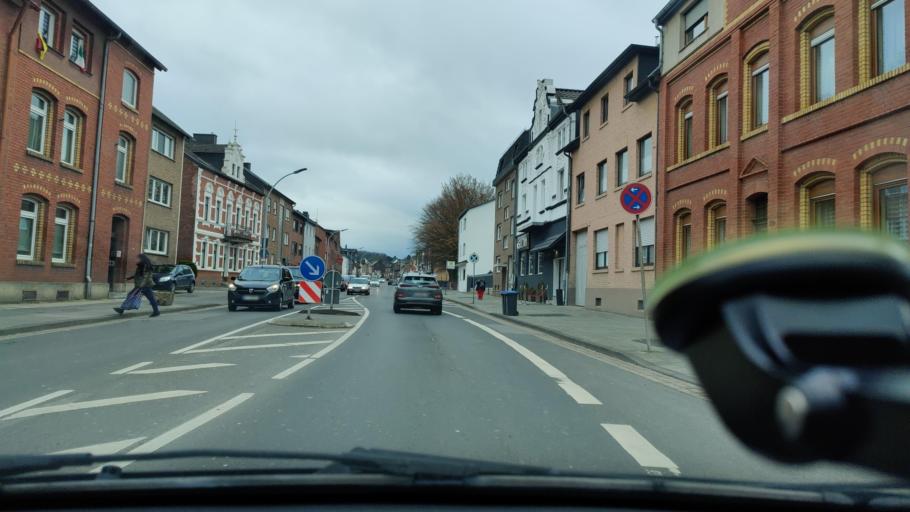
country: DE
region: North Rhine-Westphalia
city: Siersdorf
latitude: 50.8676
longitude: 6.2119
